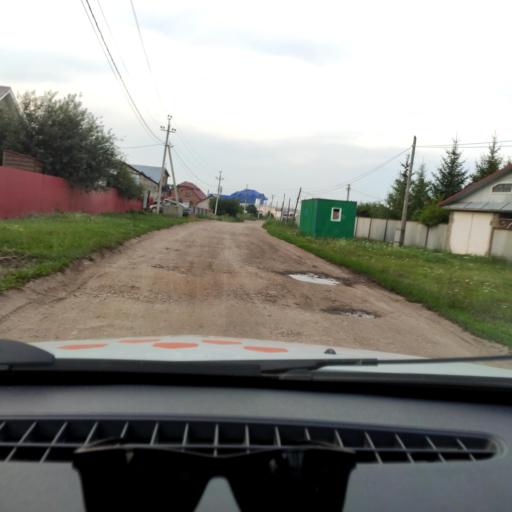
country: RU
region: Bashkortostan
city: Ufa
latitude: 54.6111
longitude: 55.9312
